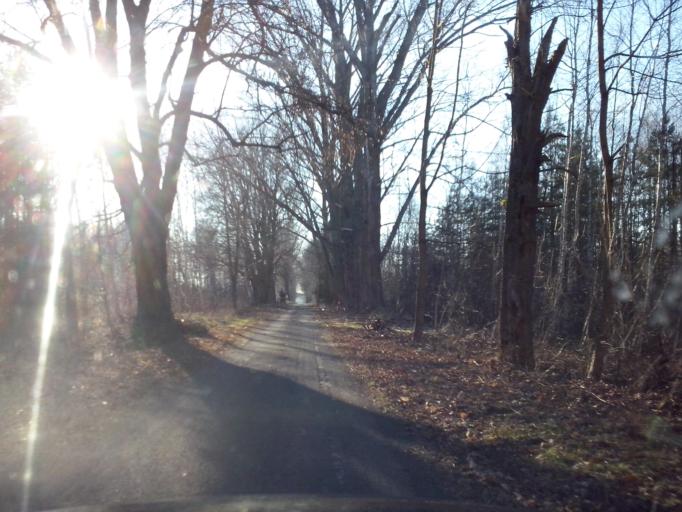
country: PL
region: Subcarpathian Voivodeship
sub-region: Powiat nizanski
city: Harasiuki
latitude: 50.5224
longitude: 22.4974
